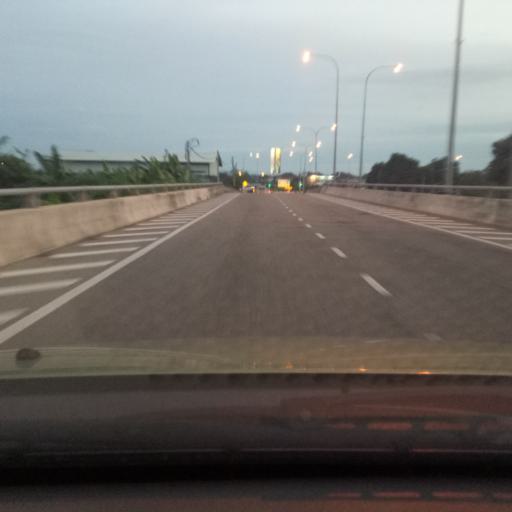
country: MY
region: Kedah
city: Alor Setar
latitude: 6.0990
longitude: 100.3736
